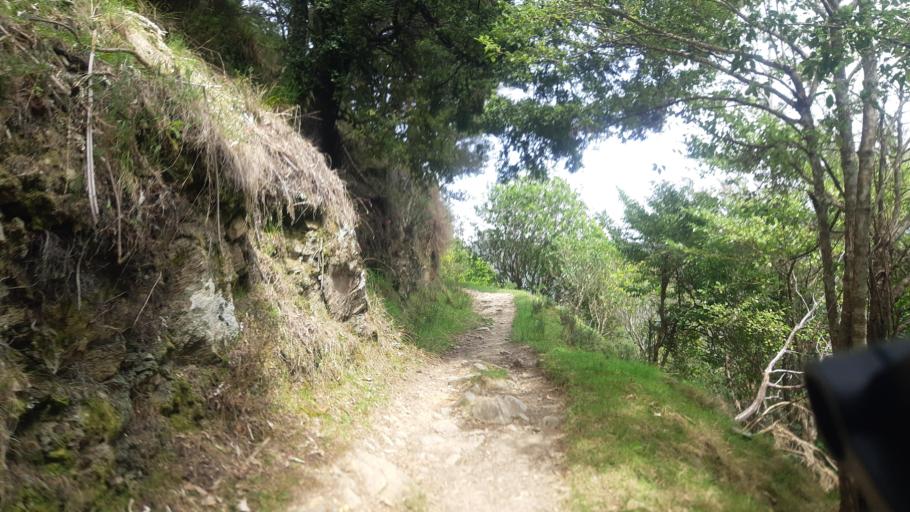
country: NZ
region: Marlborough
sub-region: Marlborough District
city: Picton
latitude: -41.2467
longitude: 173.9587
